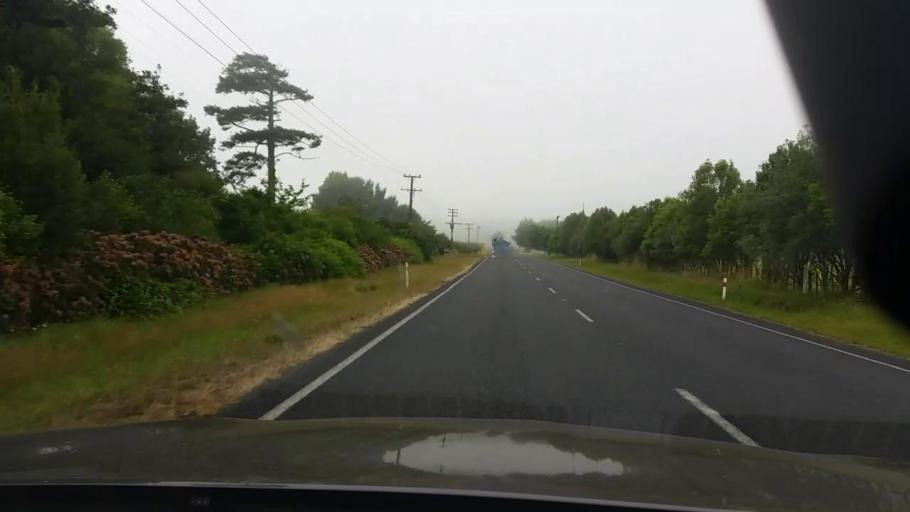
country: NZ
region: Waikato
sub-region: Hamilton City
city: Hamilton
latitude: -37.6480
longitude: 175.2973
